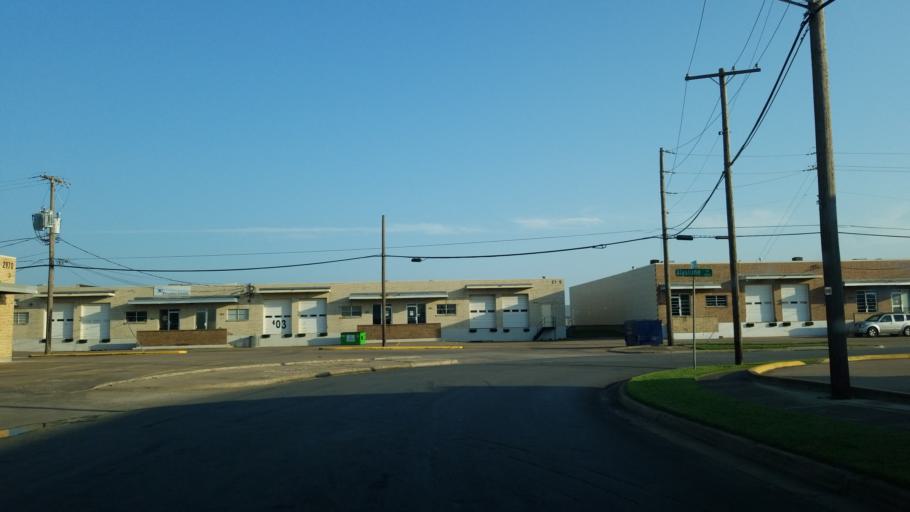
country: US
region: Texas
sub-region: Dallas County
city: Farmers Branch
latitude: 32.8741
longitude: -96.8781
